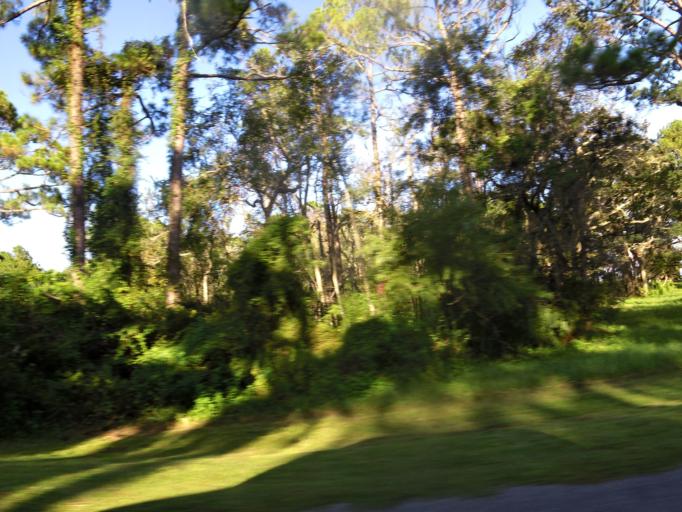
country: US
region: Florida
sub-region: Franklin County
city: Eastpoint
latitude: 29.7590
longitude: -84.8303
